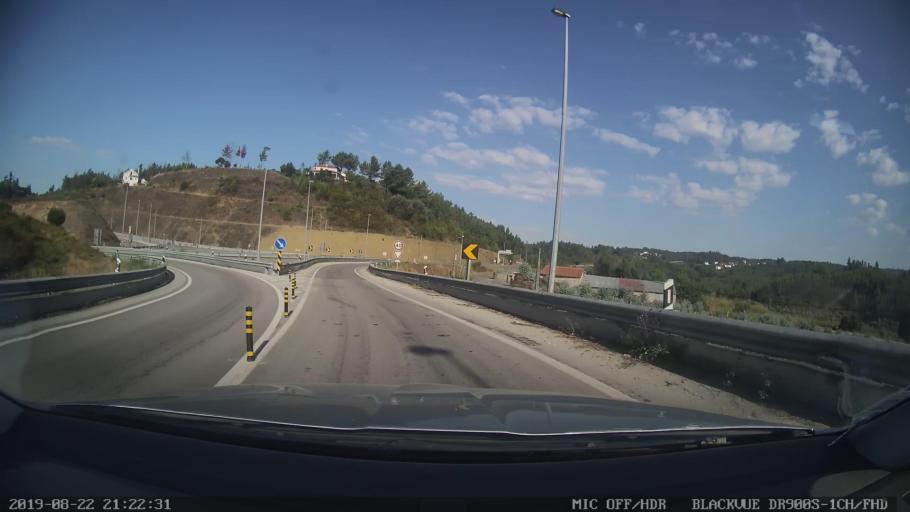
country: PT
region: Castelo Branco
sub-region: Serta
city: Serta
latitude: 39.8216
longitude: -8.1011
